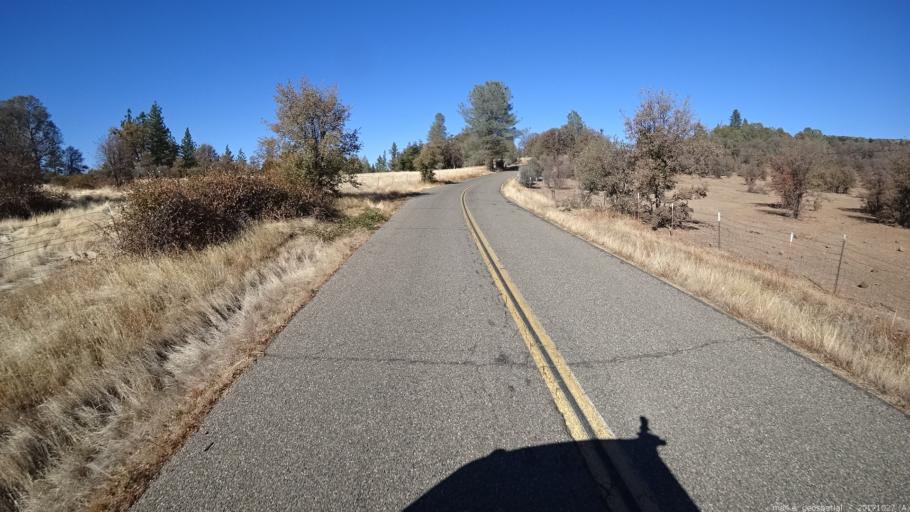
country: US
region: California
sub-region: Shasta County
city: Shingletown
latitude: 40.6443
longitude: -121.8882
